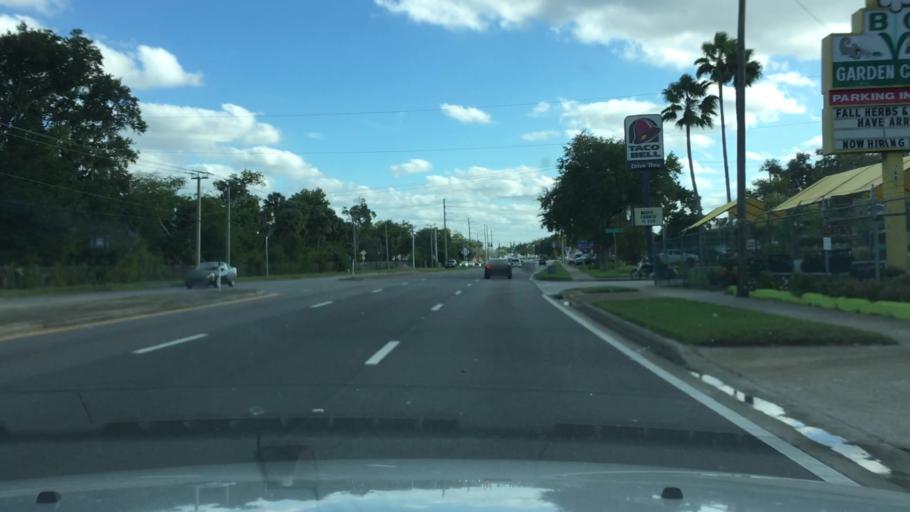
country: US
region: Florida
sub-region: Volusia County
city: Daytona Beach
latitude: 29.2190
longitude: -81.0471
